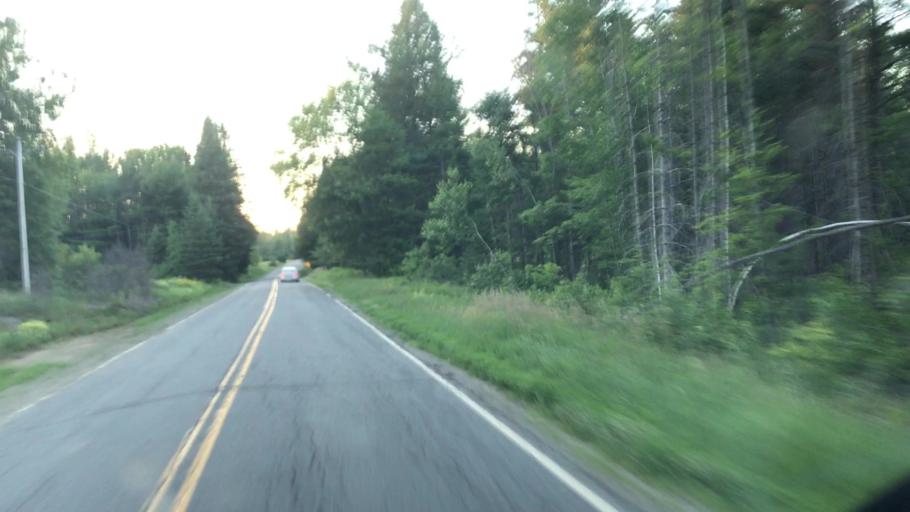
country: US
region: Maine
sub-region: Penobscot County
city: Medway
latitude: 45.6092
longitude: -68.2572
